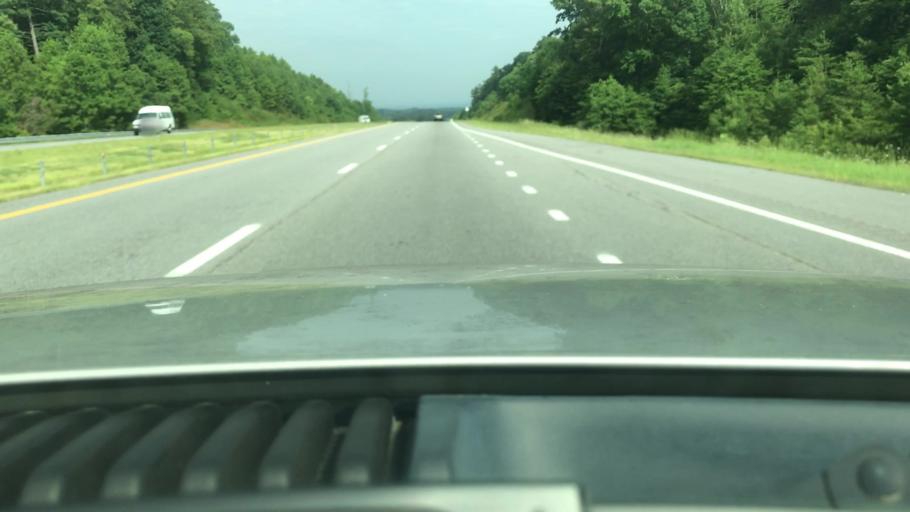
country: US
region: North Carolina
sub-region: Yadkin County
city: Jonesville
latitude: 36.1572
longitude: -80.9366
